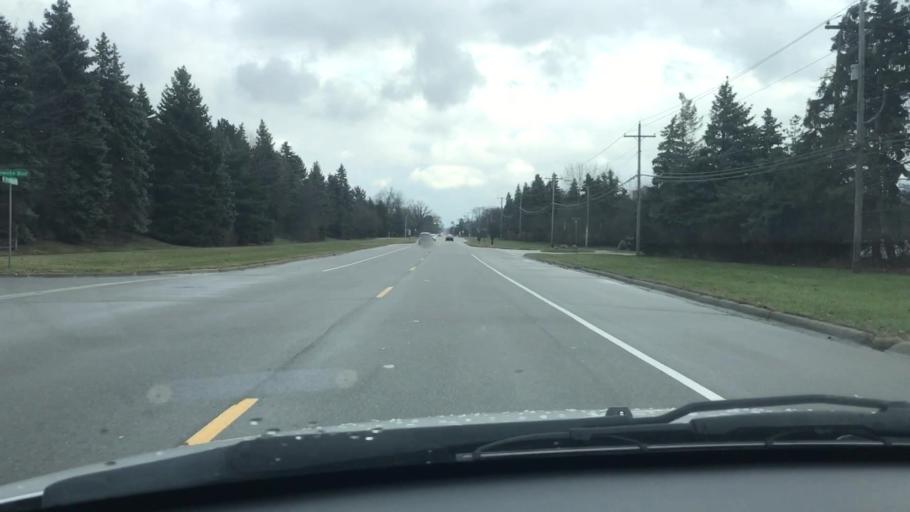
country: US
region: Michigan
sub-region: Oakland County
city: Birmingham
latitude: 42.5764
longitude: -83.1817
